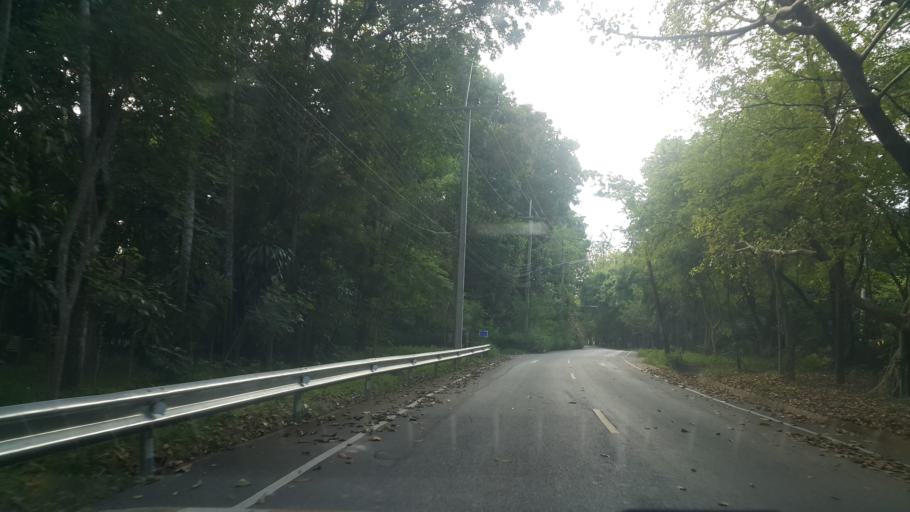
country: TH
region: Rayong
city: Ban Chang
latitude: 12.7865
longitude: 100.9608
